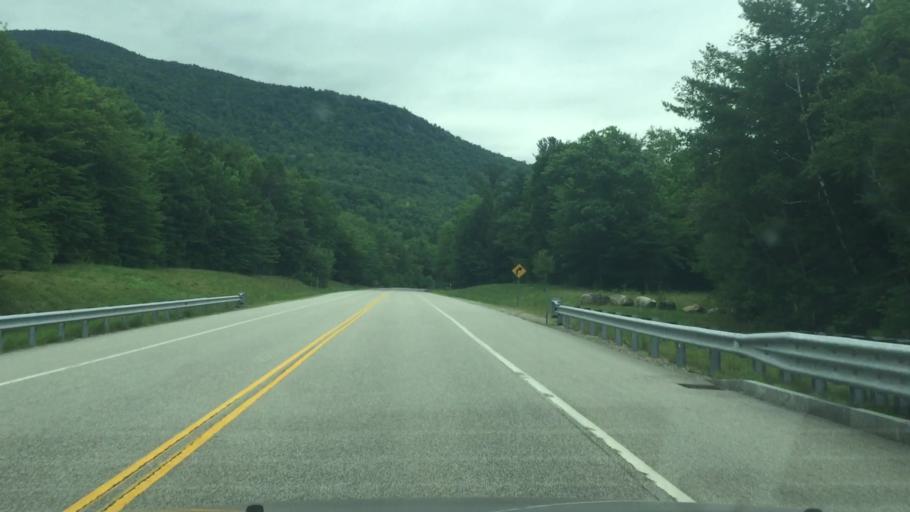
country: US
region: New Hampshire
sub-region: Carroll County
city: North Conway
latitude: 44.0854
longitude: -71.3500
